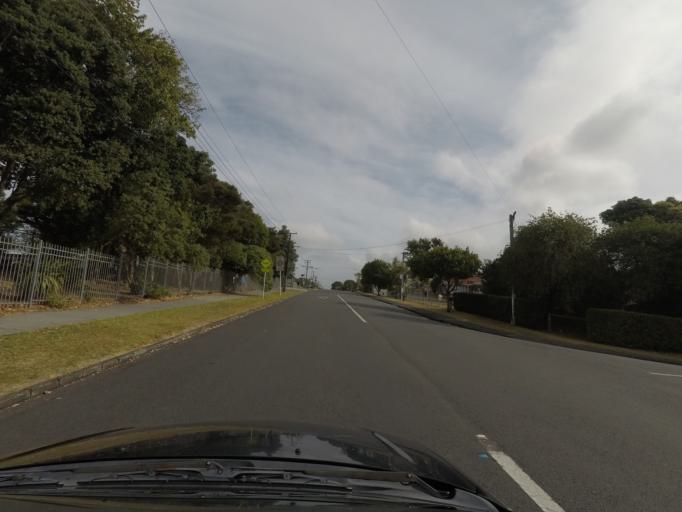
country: NZ
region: Auckland
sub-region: Auckland
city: Waitakere
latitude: -36.9026
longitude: 174.6654
